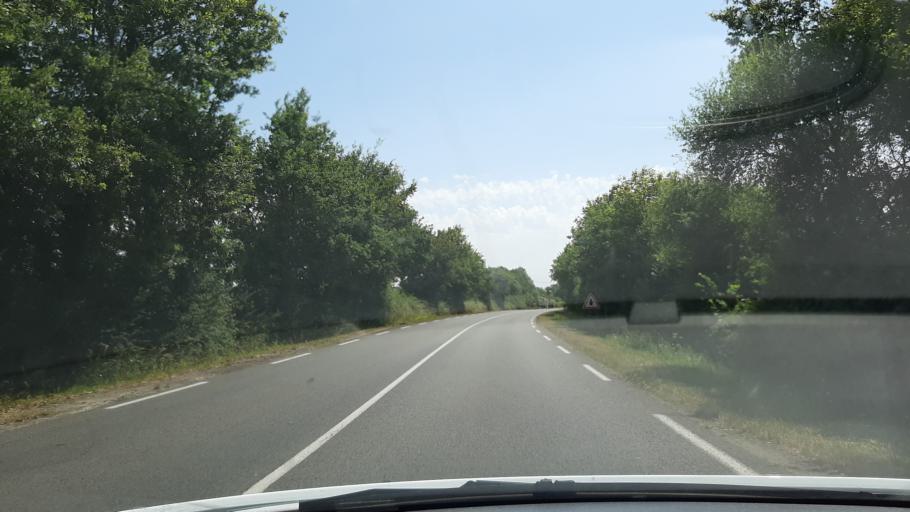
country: FR
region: Pays de la Loire
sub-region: Departement de la Vendee
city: Mouilleron-le-Captif
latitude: 46.7503
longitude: -1.4604
